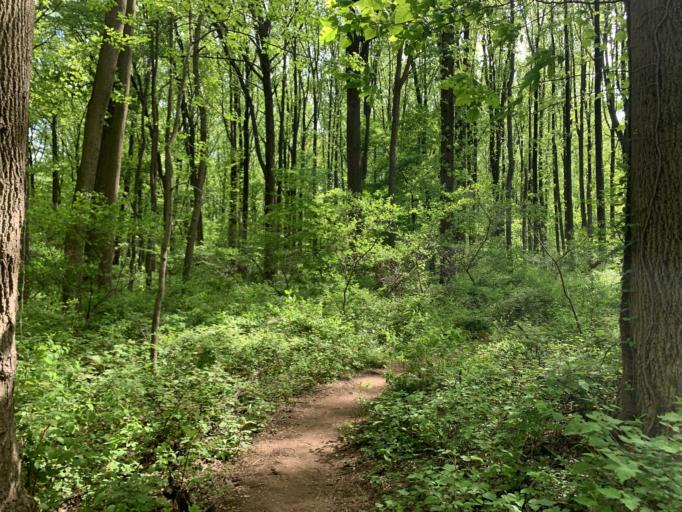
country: US
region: Maryland
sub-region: Harford County
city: South Bel Air
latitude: 39.6216
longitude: -76.2761
